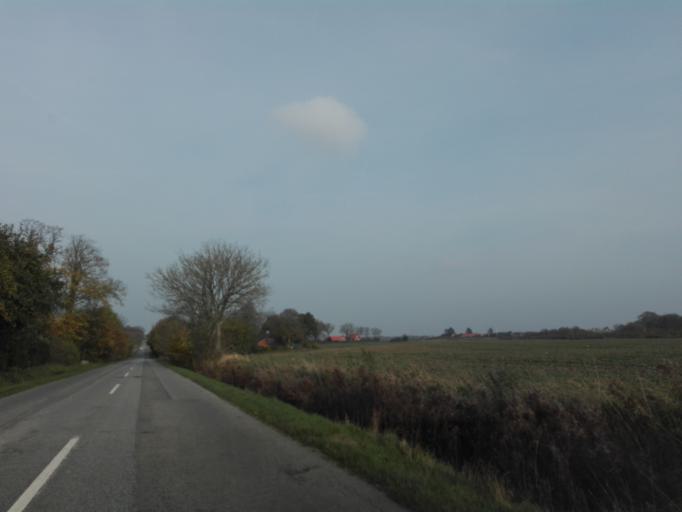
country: DK
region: Central Jutland
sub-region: Arhus Kommune
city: Solbjerg
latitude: 56.0602
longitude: 10.0910
